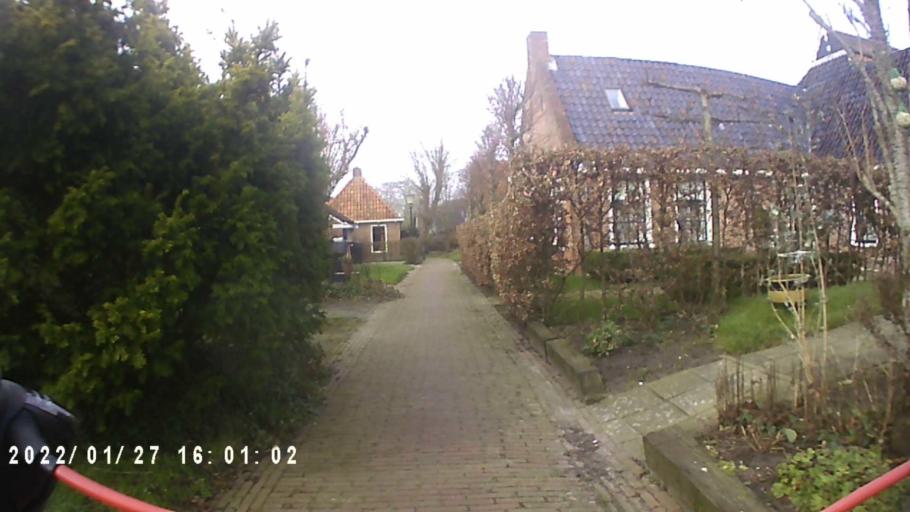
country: NL
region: Friesland
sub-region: Gemeente Dongeradeel
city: Anjum
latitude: 53.3726
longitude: 6.0886
